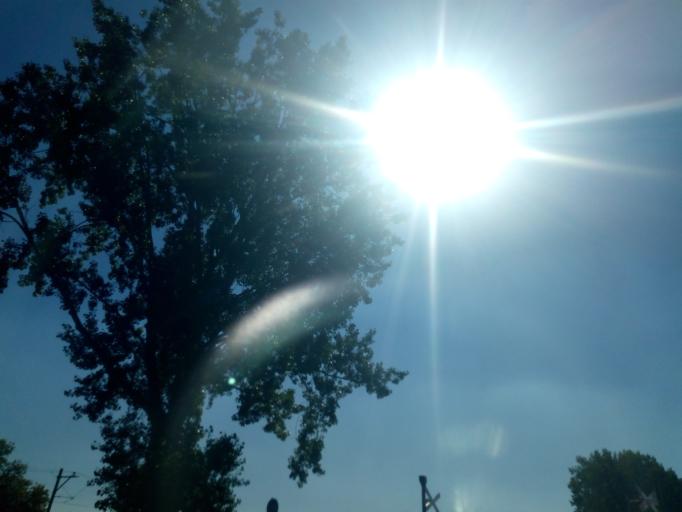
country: NL
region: South Holland
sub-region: Gemeente Alphen aan den Rijn
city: Alphen aan den Rijn
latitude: 52.1306
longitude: 4.6390
